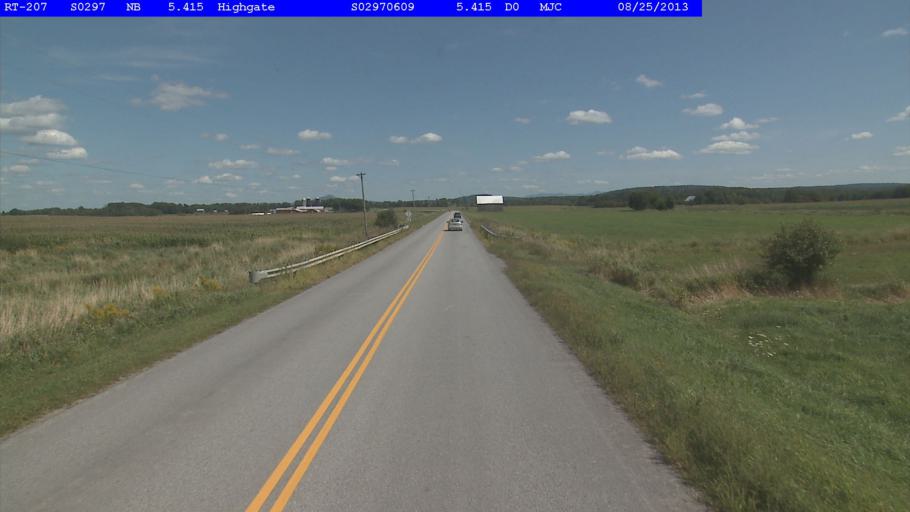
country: CA
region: Quebec
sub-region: Monteregie
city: Bedford
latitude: 45.0054
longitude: -72.9984
